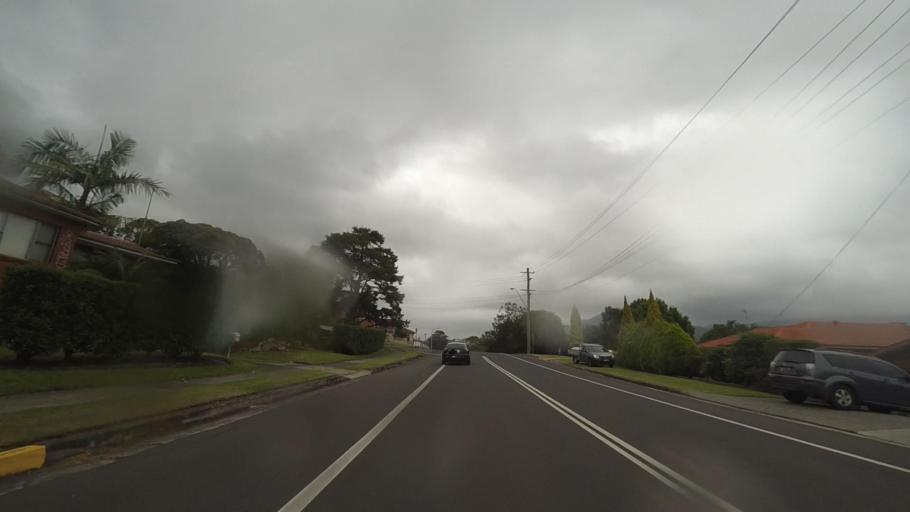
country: AU
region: New South Wales
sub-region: Wollongong
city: Cordeaux Heights
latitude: -34.4415
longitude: 150.8483
